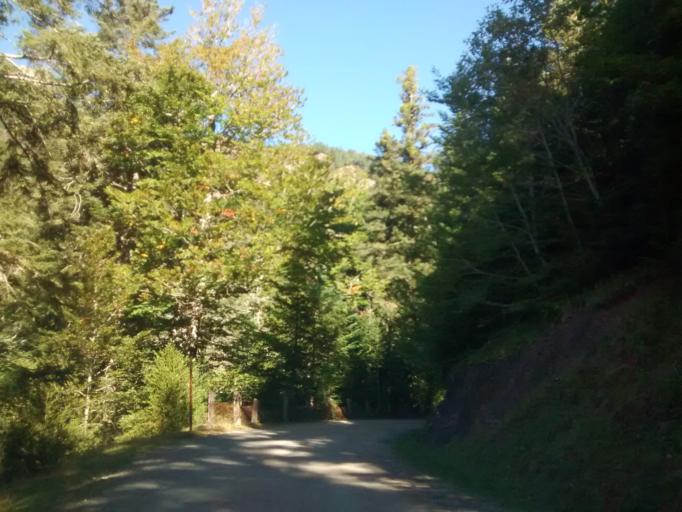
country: ES
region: Aragon
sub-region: Provincia de Huesca
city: Aragues del Puerto
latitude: 42.8433
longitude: -0.7104
